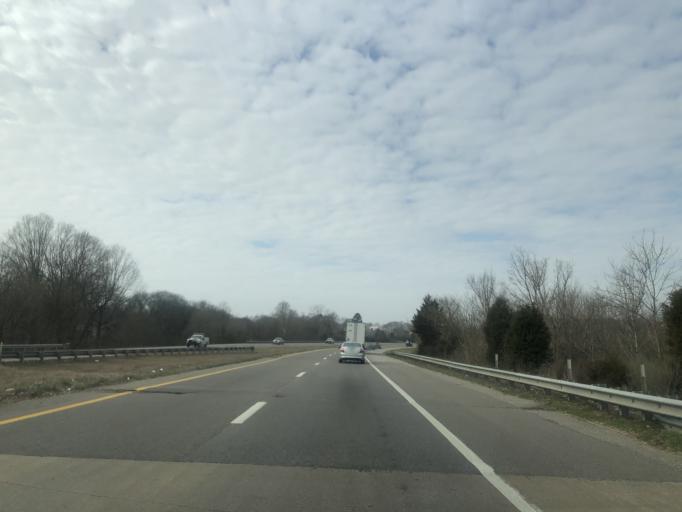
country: US
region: Tennessee
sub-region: Maury County
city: Columbia
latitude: 35.6377
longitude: -87.0357
